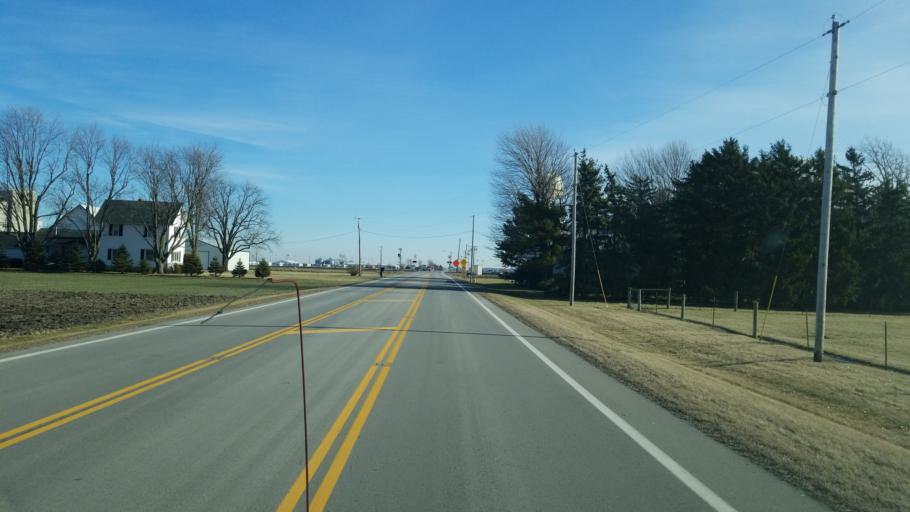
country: US
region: Ohio
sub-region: Putnam County
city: Leipsic
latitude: 41.1236
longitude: -83.9668
